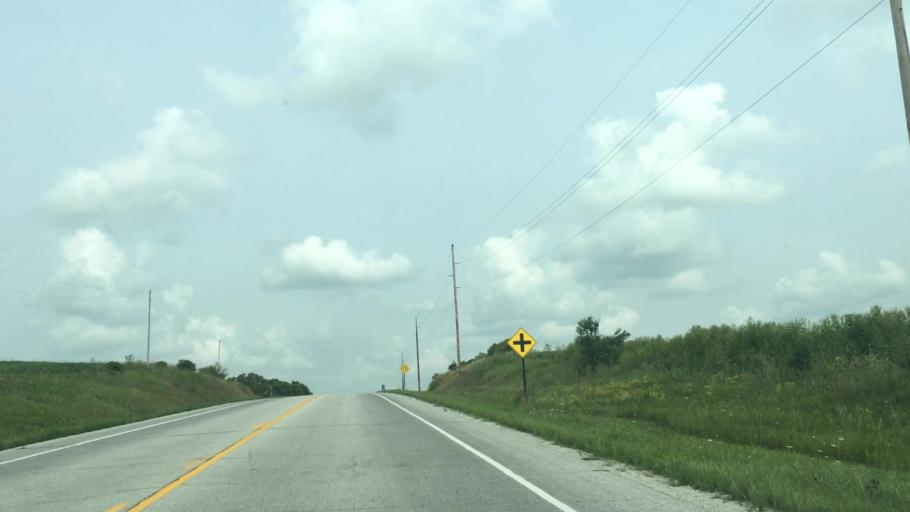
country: US
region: Minnesota
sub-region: Fillmore County
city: Harmony
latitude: 43.5780
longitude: -91.9298
